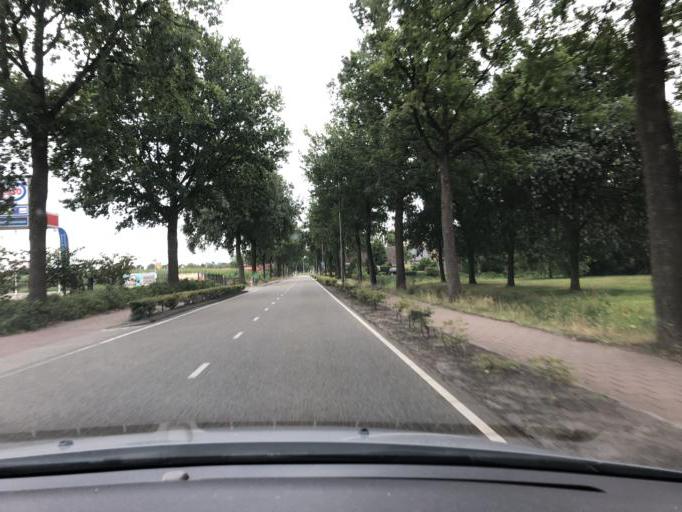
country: NL
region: Overijssel
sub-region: Gemeente Dalfsen
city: Dalfsen
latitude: 52.5868
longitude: 6.2847
